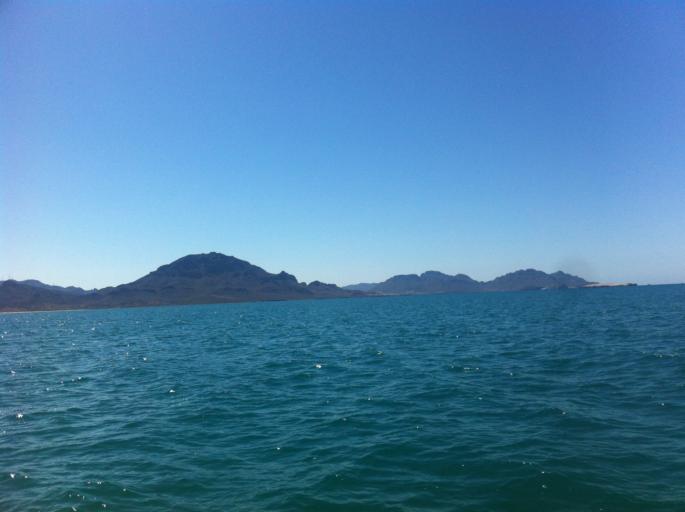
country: MX
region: Sonora
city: Heroica Guaymas
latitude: 27.9629
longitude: -111.0087
